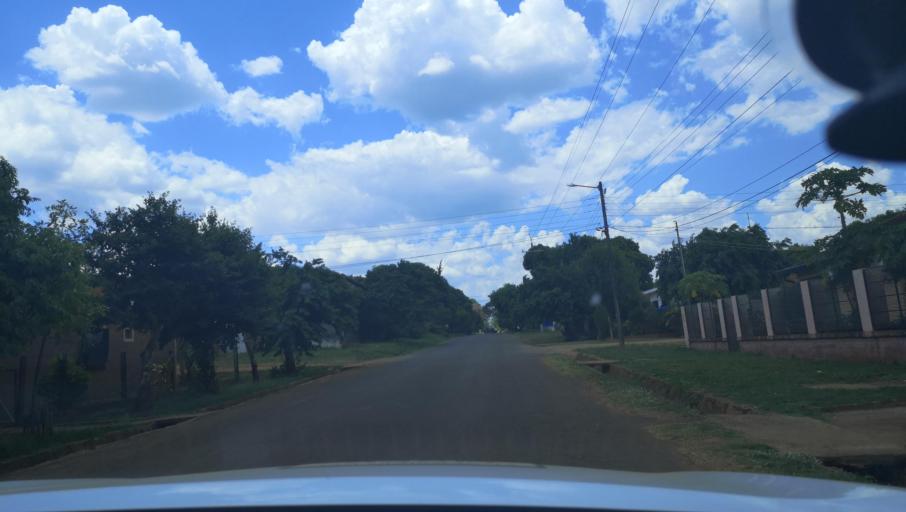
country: PY
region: Itapua
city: Carmen del Parana
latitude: -27.1708
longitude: -56.2385
